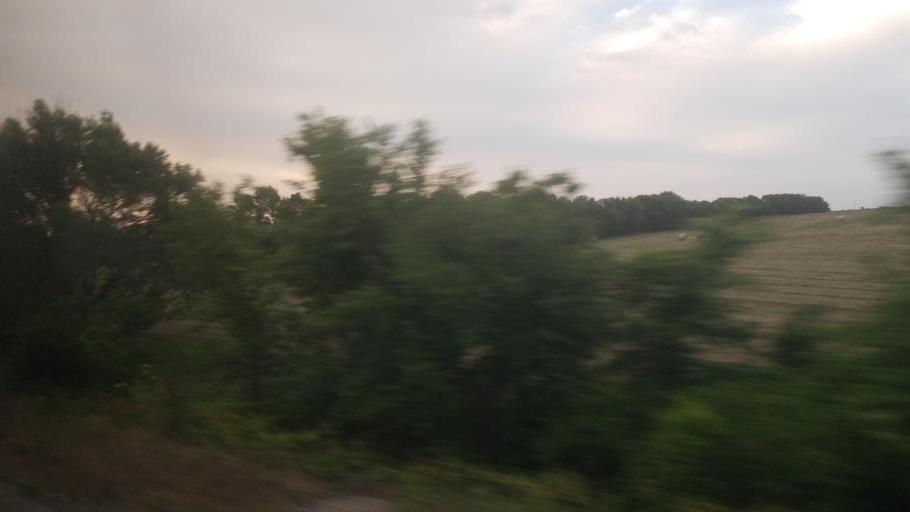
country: US
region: Kansas
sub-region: Marion County
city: Peabody
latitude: 38.1652
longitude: -97.0865
